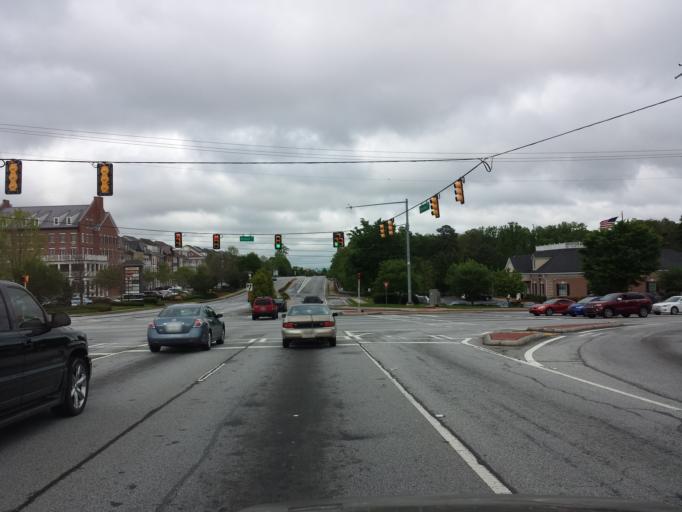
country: US
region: Georgia
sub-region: Cobb County
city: Vinings
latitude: 33.8487
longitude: -84.4936
